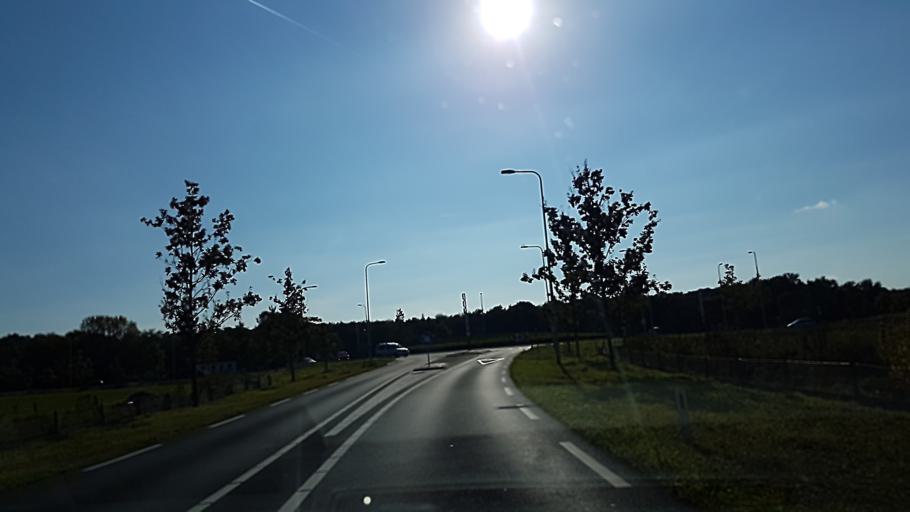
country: NL
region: North Brabant
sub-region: Gemeente Woensdrecht
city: Woensdrecht
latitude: 51.4157
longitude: 4.3399
